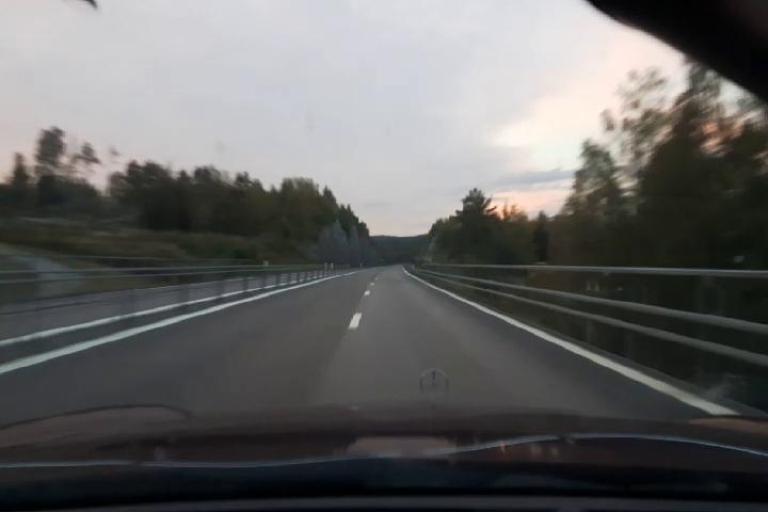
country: SE
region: Vaesternorrland
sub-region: Haernoesands Kommun
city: Haernoesand
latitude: 62.8327
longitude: 17.9677
